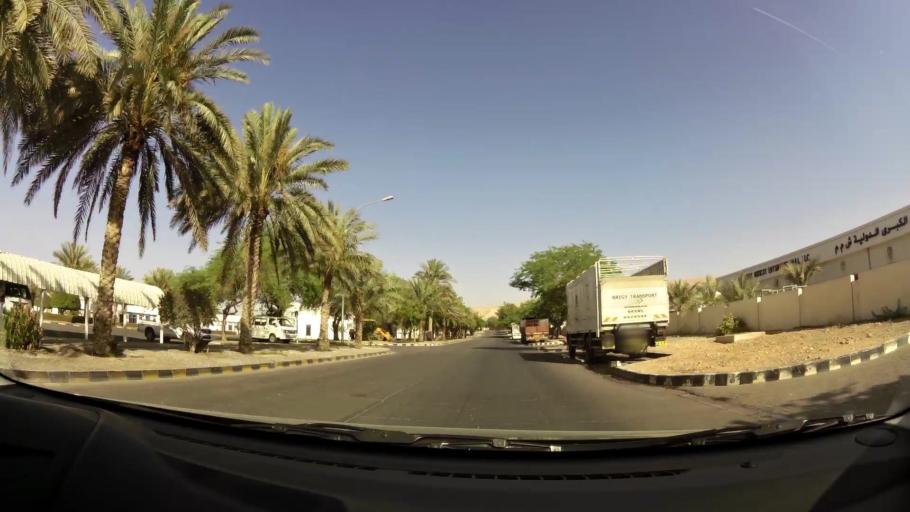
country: OM
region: Muhafazat Masqat
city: As Sib al Jadidah
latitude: 23.5559
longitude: 58.2031
